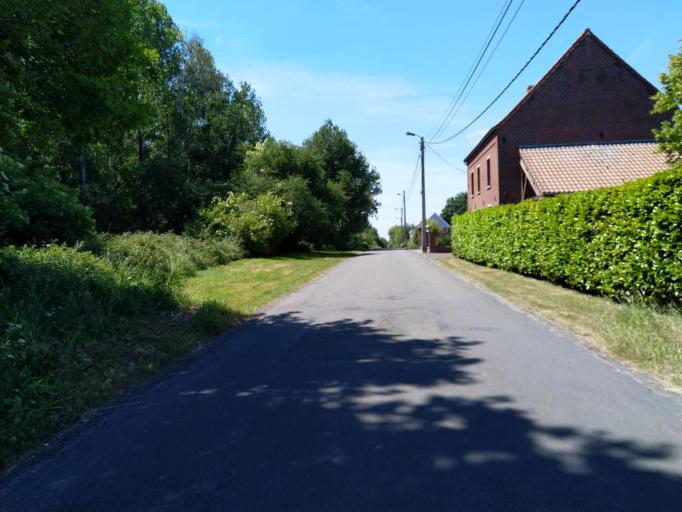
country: BE
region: Wallonia
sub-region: Province du Hainaut
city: Saint-Ghislain
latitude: 50.5085
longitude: 3.8410
